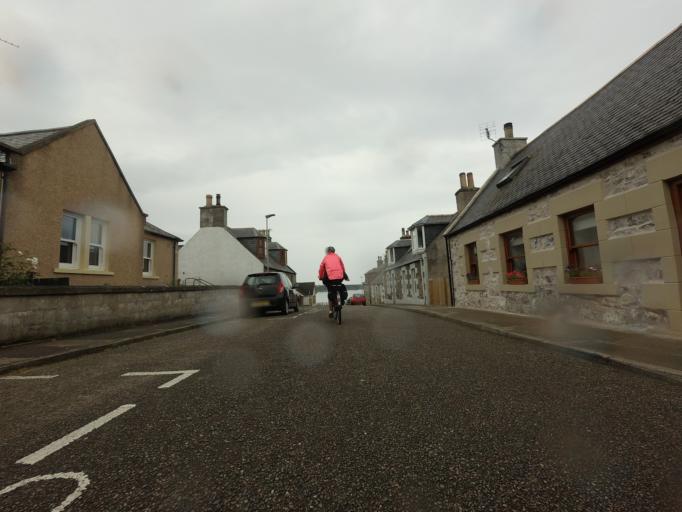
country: GB
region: Scotland
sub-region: Moray
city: Cullen
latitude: 57.6903
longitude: -2.8222
